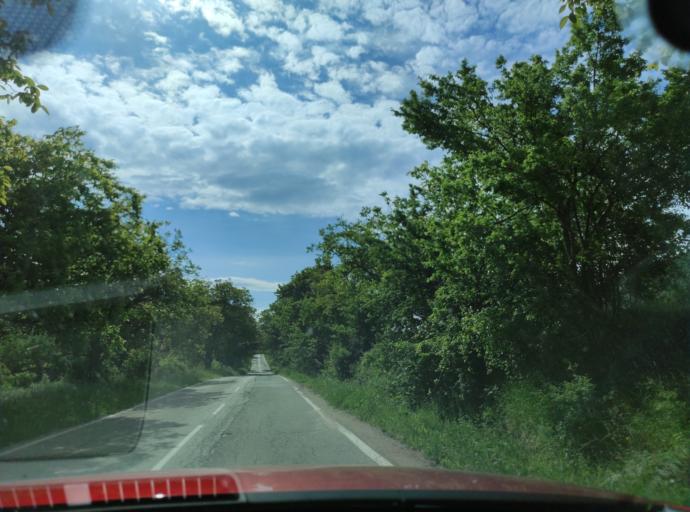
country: BG
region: Montana
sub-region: Obshtina Chiprovtsi
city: Chiprovtsi
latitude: 43.4841
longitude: 22.8219
